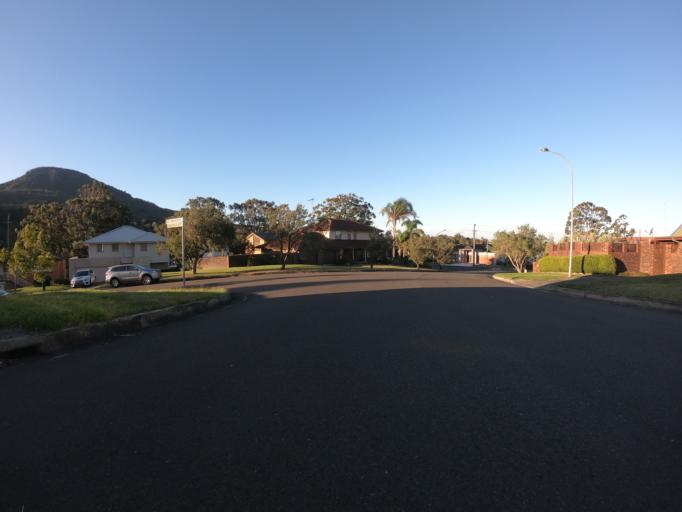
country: AU
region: New South Wales
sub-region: Wollongong
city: Mount Keira
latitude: -34.4212
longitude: 150.8546
